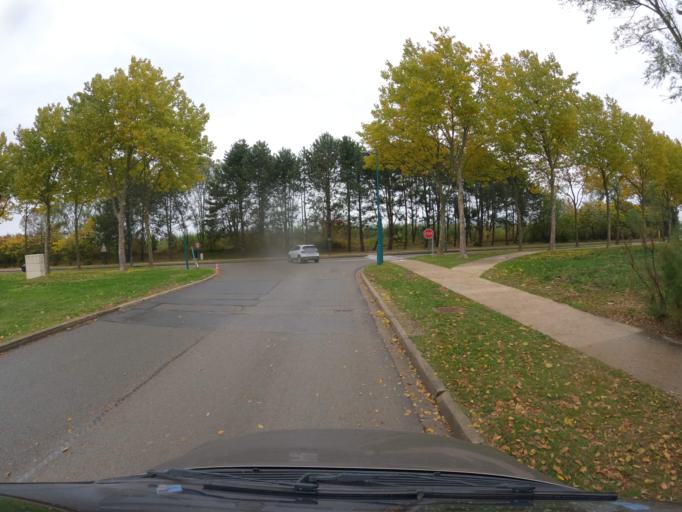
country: FR
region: Ile-de-France
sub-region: Departement de Seine-et-Marne
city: Serris
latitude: 48.8616
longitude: 2.7863
